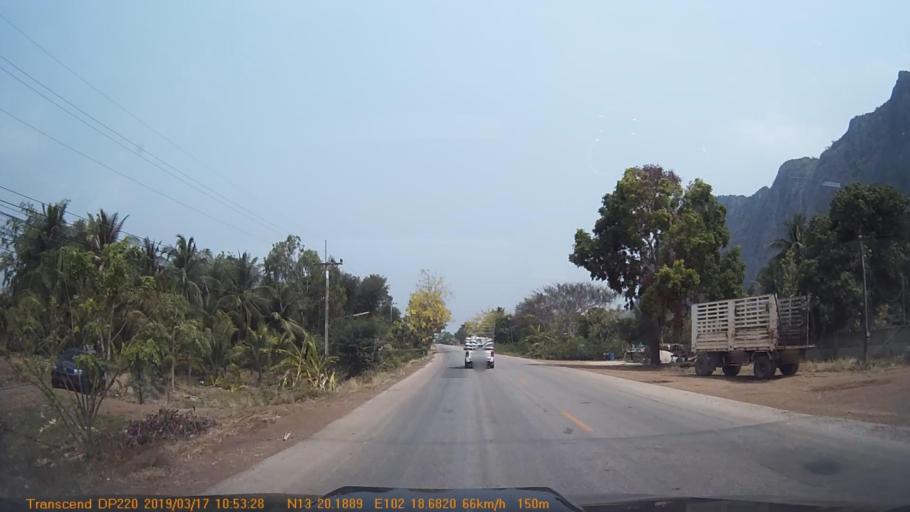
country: TH
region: Sa Kaeo
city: Khlong Hat
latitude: 13.3369
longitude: 102.3113
